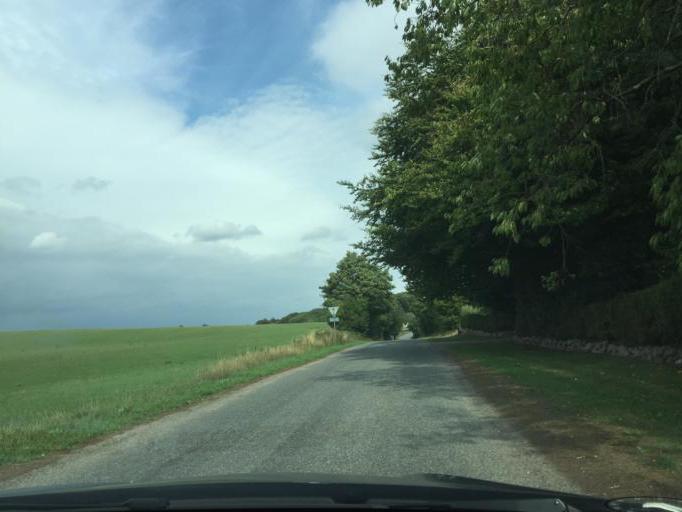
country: DK
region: South Denmark
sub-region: Assens Kommune
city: Vissenbjerg
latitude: 55.3966
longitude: 10.1652
